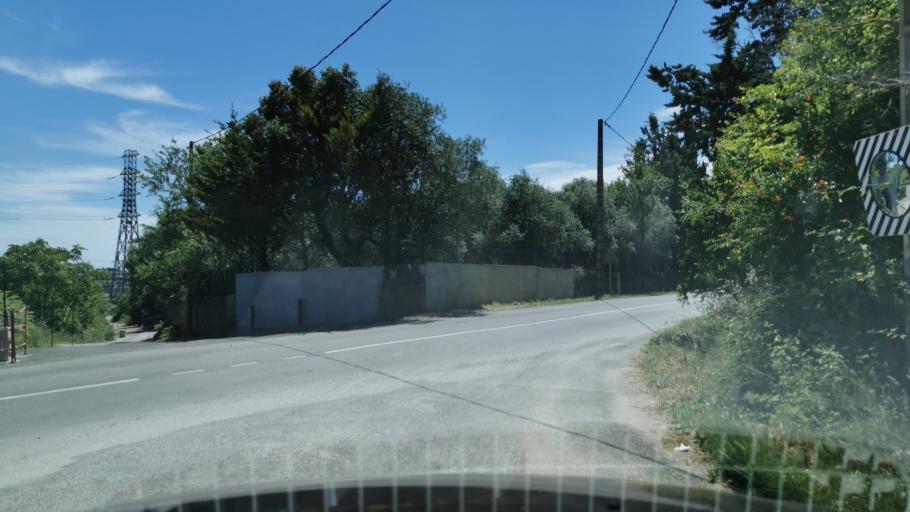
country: FR
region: Languedoc-Roussillon
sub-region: Departement de l'Aude
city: Narbonne
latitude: 43.1993
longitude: 2.9804
